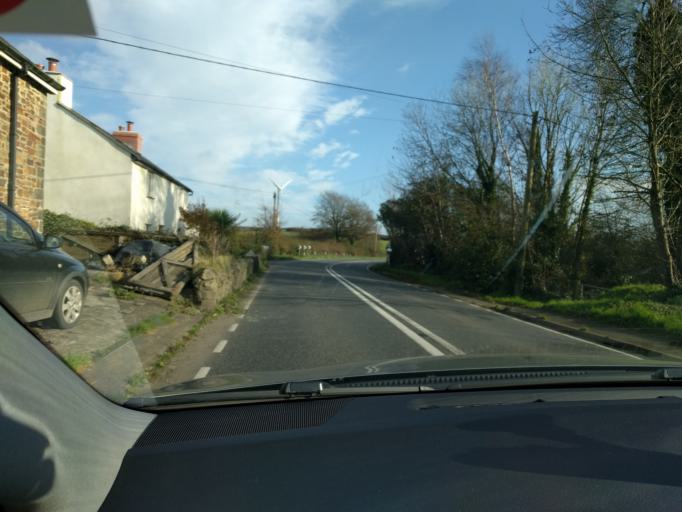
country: GB
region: England
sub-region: Cornwall
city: Trewen
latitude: 50.6309
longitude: -4.4609
